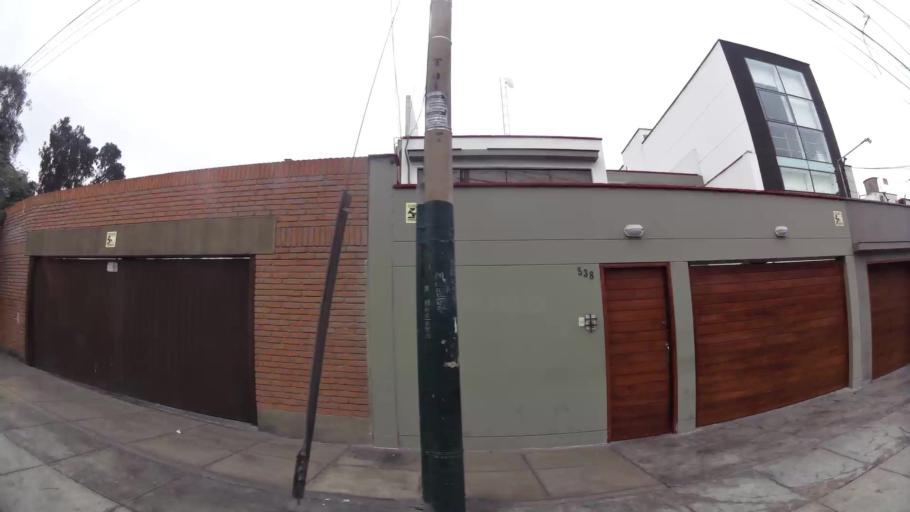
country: PE
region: Lima
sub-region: Lima
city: Surco
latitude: -12.1252
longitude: -76.9948
